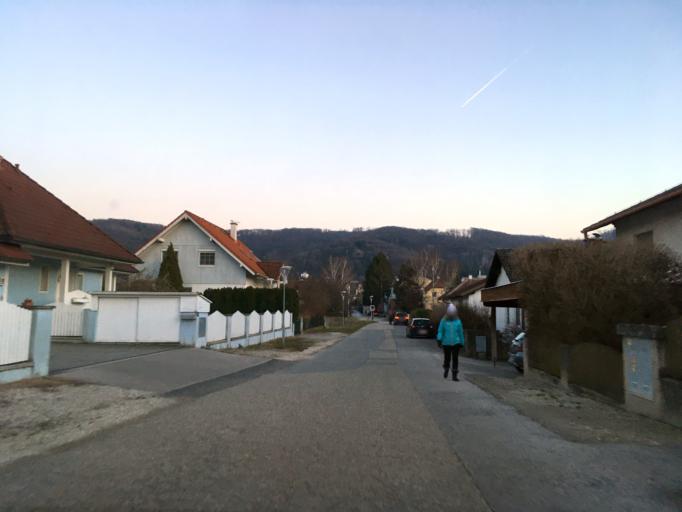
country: AT
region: Lower Austria
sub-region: Politischer Bezirk Tulln
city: Wordern
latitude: 48.3326
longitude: 16.2140
